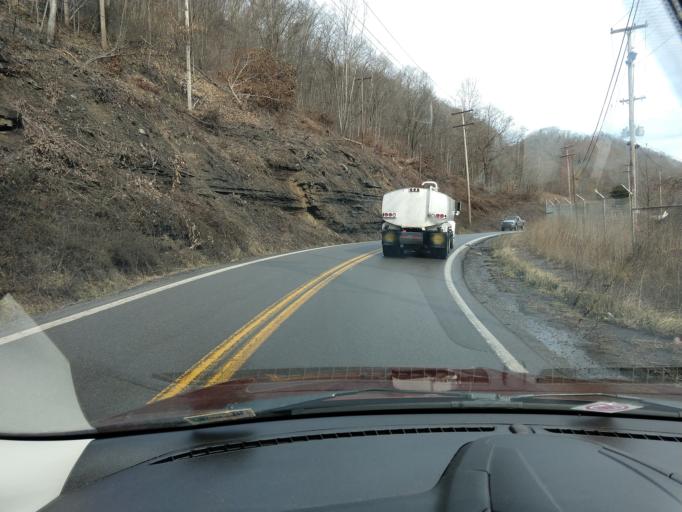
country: US
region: West Virginia
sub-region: McDowell County
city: Welch
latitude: 37.3337
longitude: -81.6808
